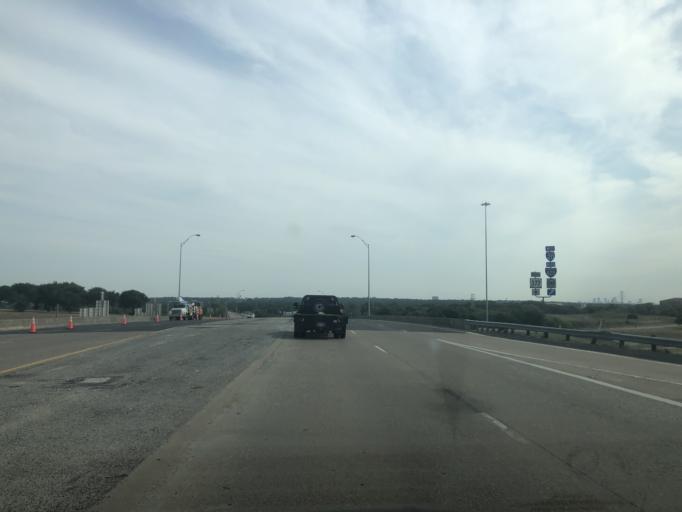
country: US
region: Texas
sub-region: Tarrant County
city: Benbrook
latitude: 32.6834
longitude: -97.4601
